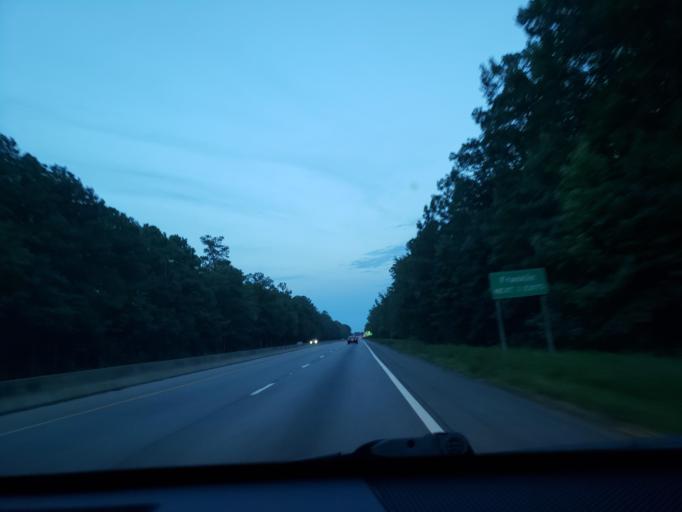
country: US
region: Virginia
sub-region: City of Franklin
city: Franklin
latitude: 36.6735
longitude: -76.9768
